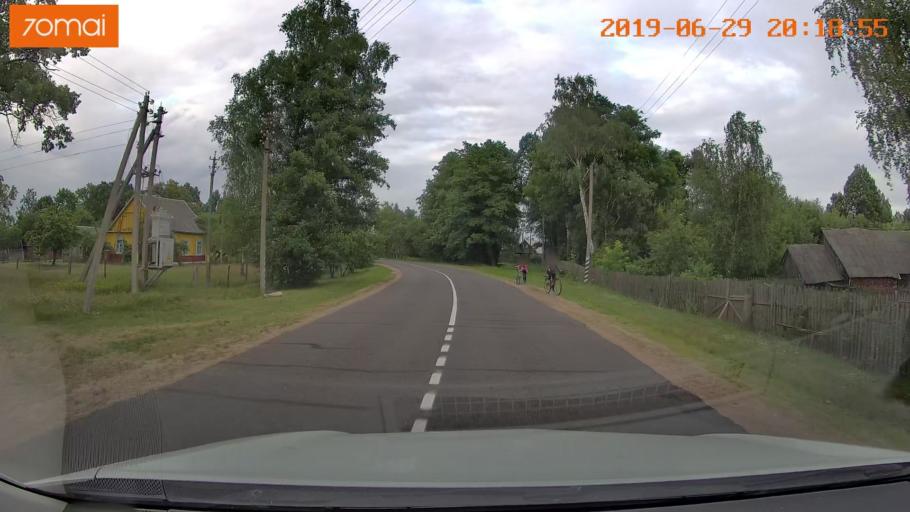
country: BY
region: Brest
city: Asnyezhytsy
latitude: 52.3968
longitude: 26.2417
